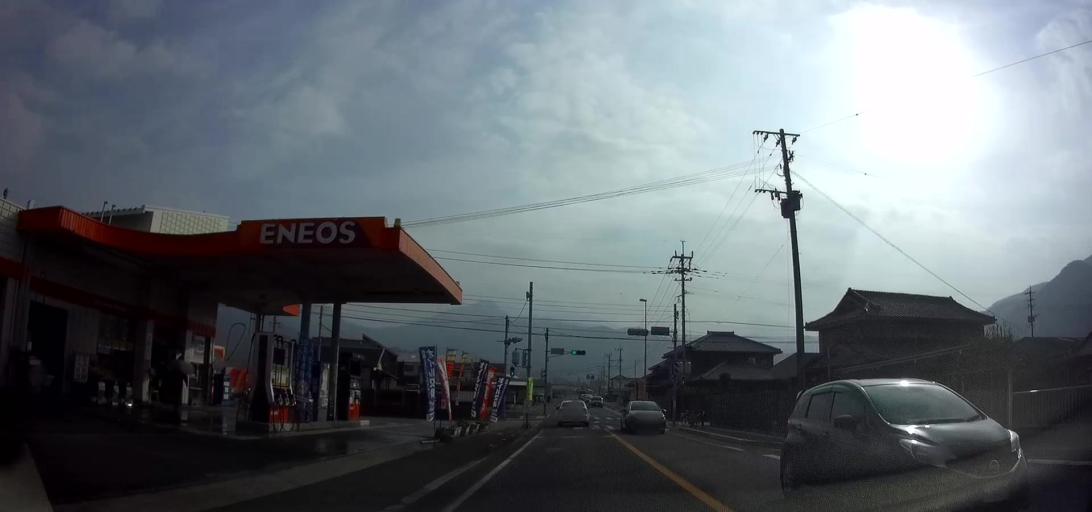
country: JP
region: Nagasaki
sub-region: Isahaya-shi
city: Isahaya
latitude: 32.7880
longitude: 130.1920
